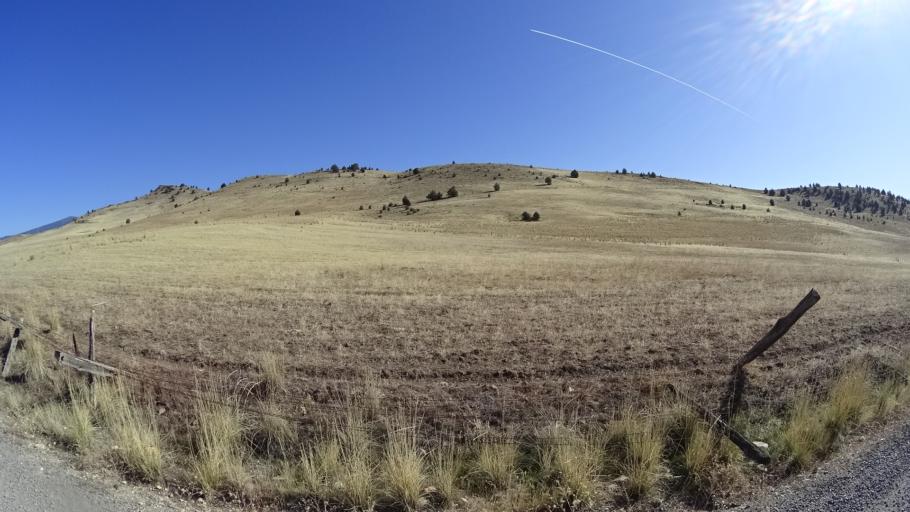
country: US
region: California
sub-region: Siskiyou County
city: Montague
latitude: 41.7386
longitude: -122.3682
